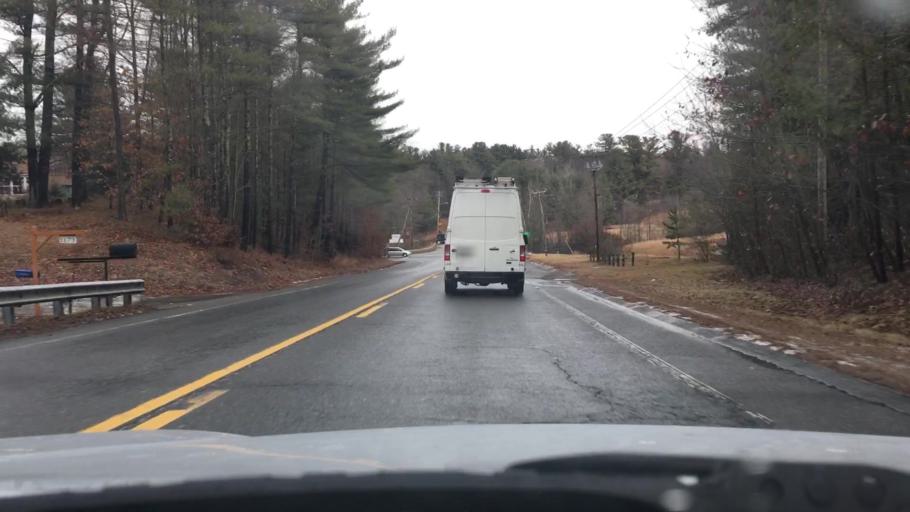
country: US
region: Massachusetts
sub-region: Franklin County
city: Orange
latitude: 42.5682
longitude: -72.2737
